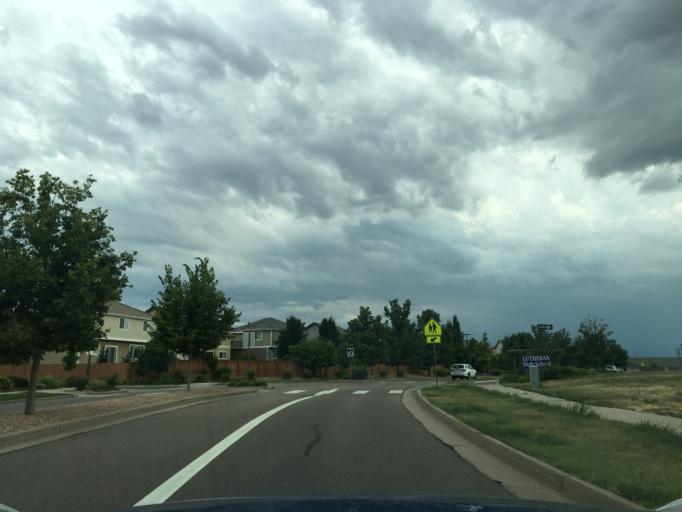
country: US
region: Colorado
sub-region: Douglas County
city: Stonegate
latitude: 39.5141
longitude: -104.8052
